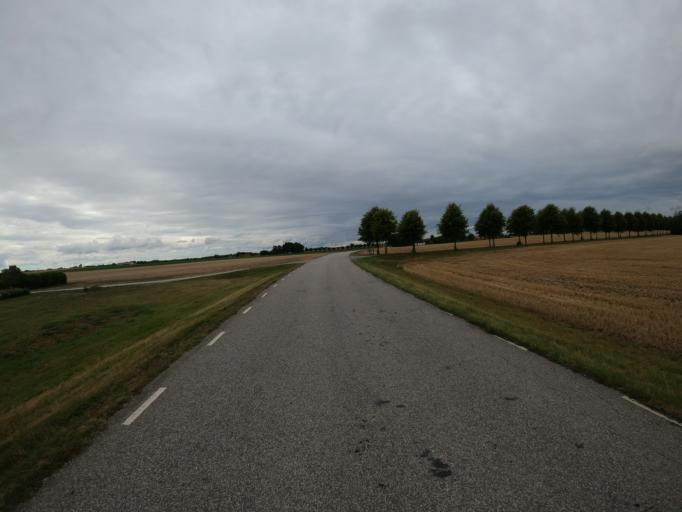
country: SE
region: Skane
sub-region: Lunds Kommun
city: Lund
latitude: 55.7549
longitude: 13.1725
